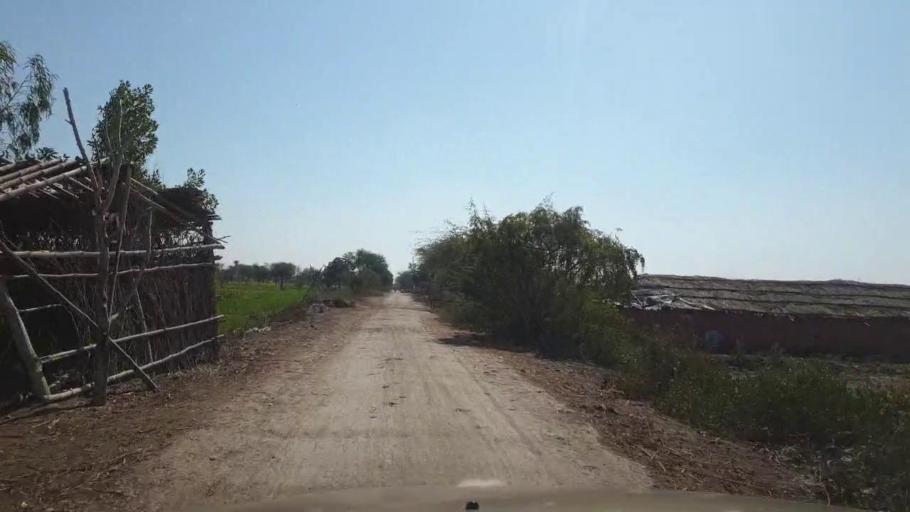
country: PK
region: Sindh
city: Mirpur Khas
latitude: 25.5577
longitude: 69.0651
